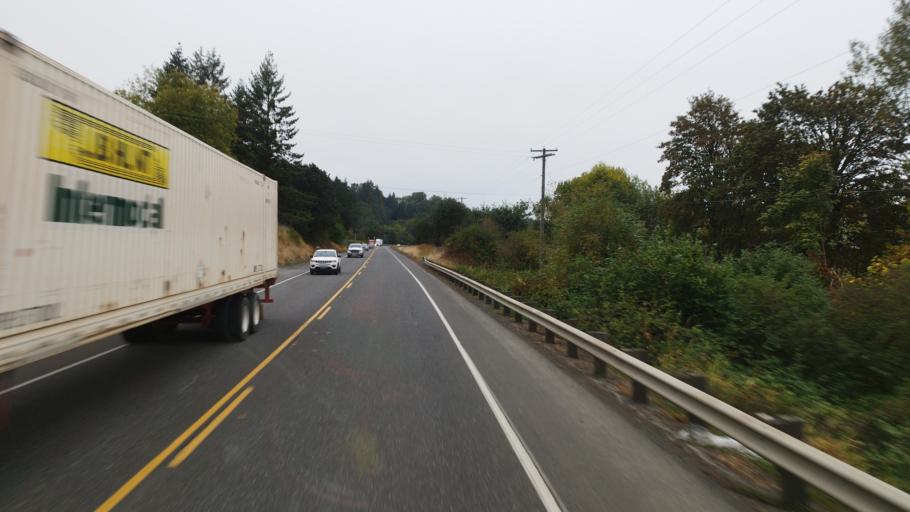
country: US
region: Washington
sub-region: Cowlitz County
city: Kalama
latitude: 45.9419
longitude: -122.8549
